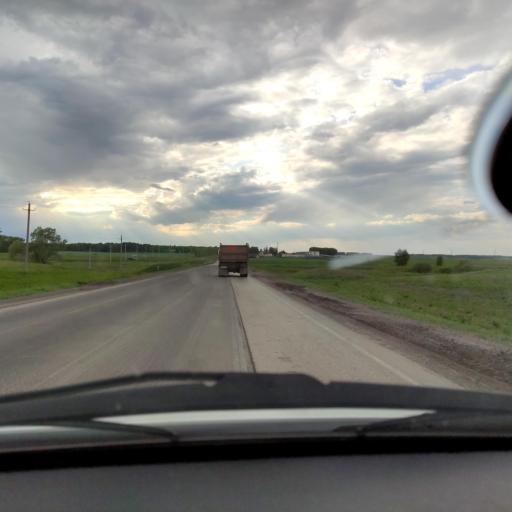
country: RU
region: Bashkortostan
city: Dyurtyuli
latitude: 55.3460
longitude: 54.9287
